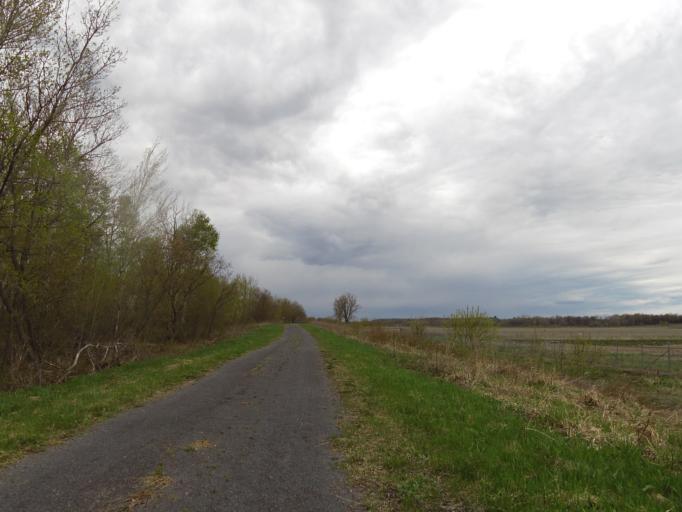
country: CA
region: Quebec
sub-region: Outaouais
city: Papineauville
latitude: 45.5321
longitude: -74.8873
